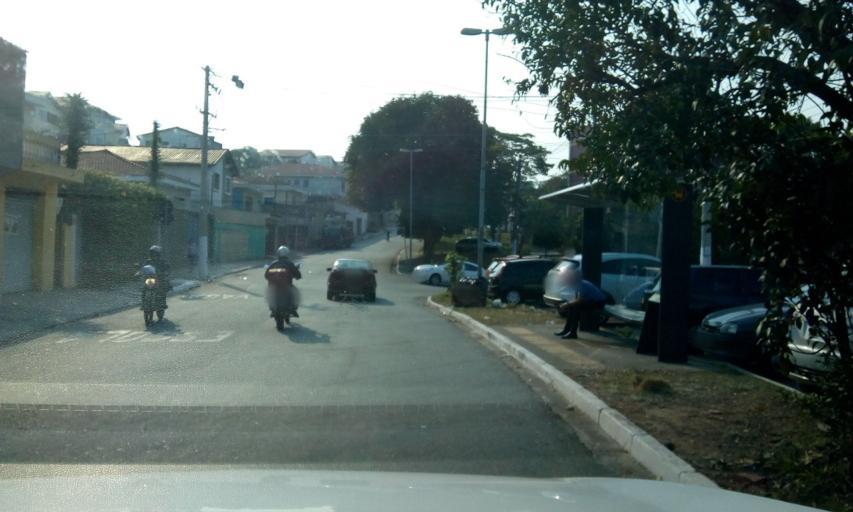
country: BR
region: Sao Paulo
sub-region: Diadema
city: Diadema
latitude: -23.7129
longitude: -46.6916
